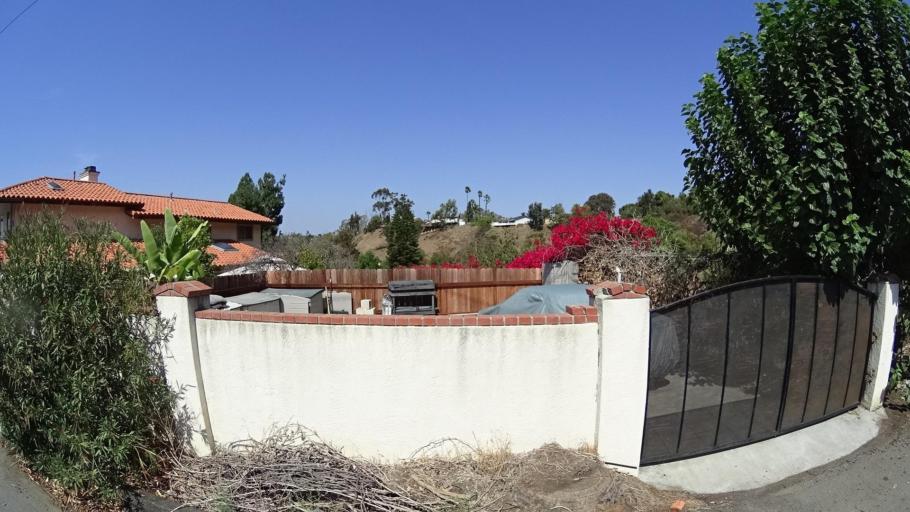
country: US
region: California
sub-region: San Diego County
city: Spring Valley
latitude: 32.7406
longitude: -116.9865
